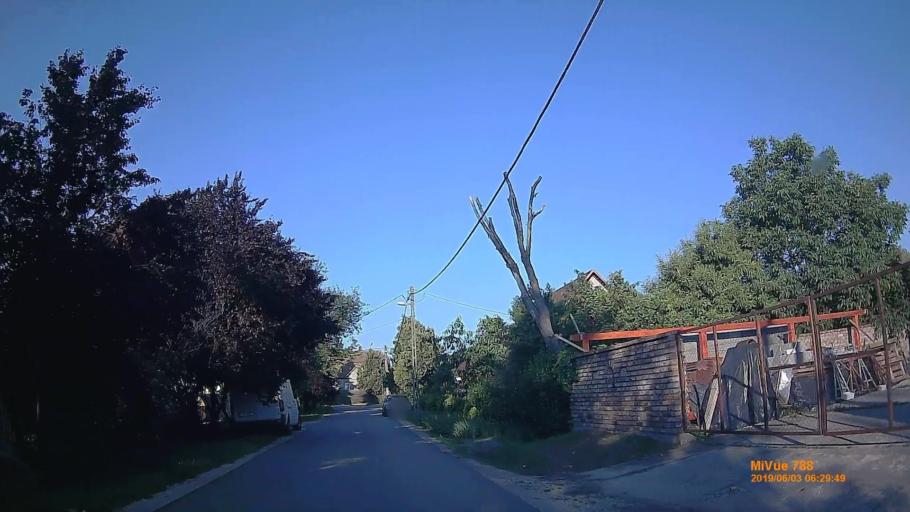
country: HU
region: Pest
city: Dunavarsany
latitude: 47.2748
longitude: 19.0689
